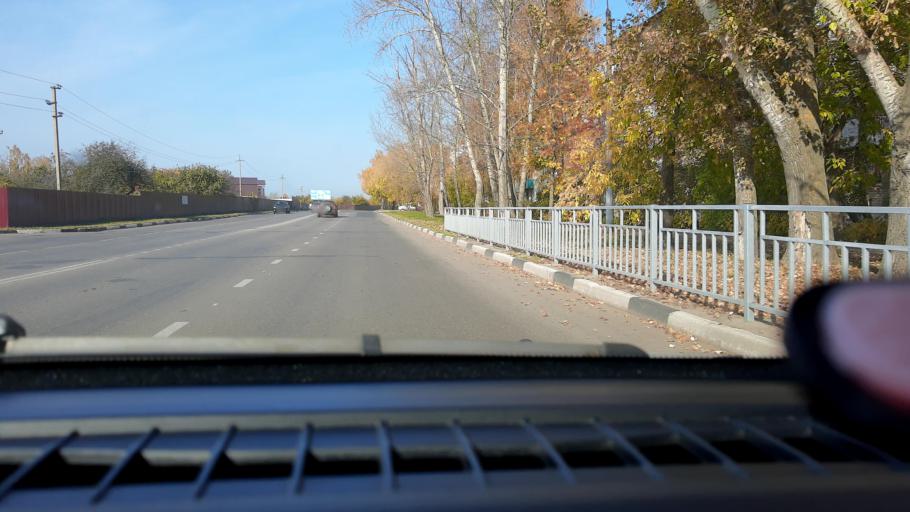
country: RU
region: Nizjnij Novgorod
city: Kstovo
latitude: 56.1430
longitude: 44.1820
